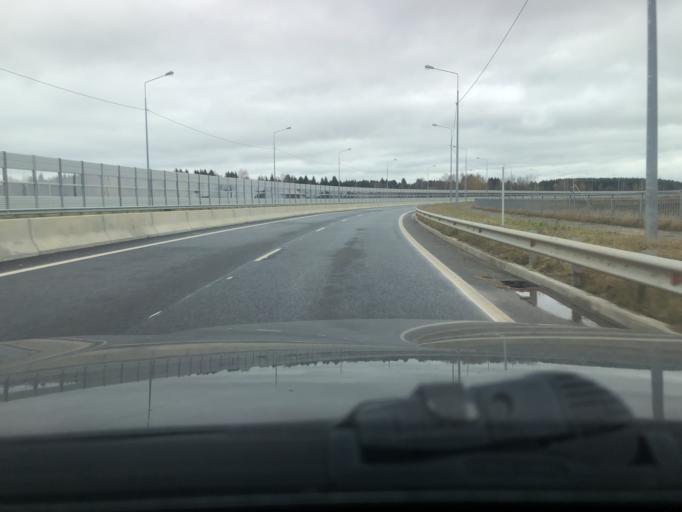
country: RU
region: Moskovskaya
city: Sergiyev Posad
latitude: 56.3377
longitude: 38.0957
